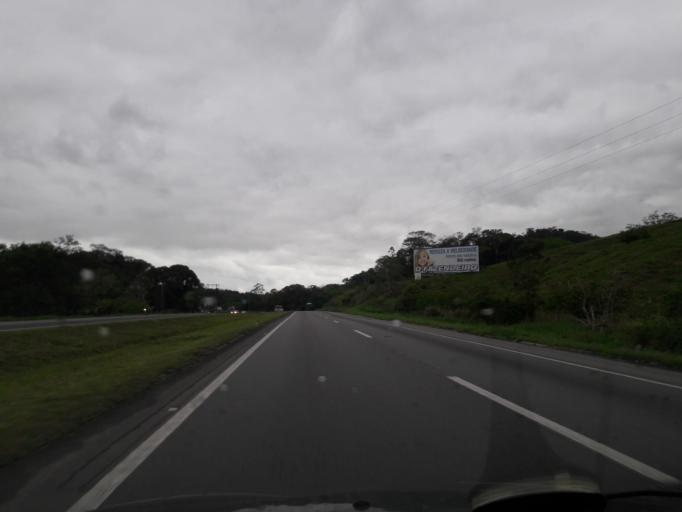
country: BR
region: Sao Paulo
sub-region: Miracatu
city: Miracatu
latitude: -24.2640
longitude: -47.3830
